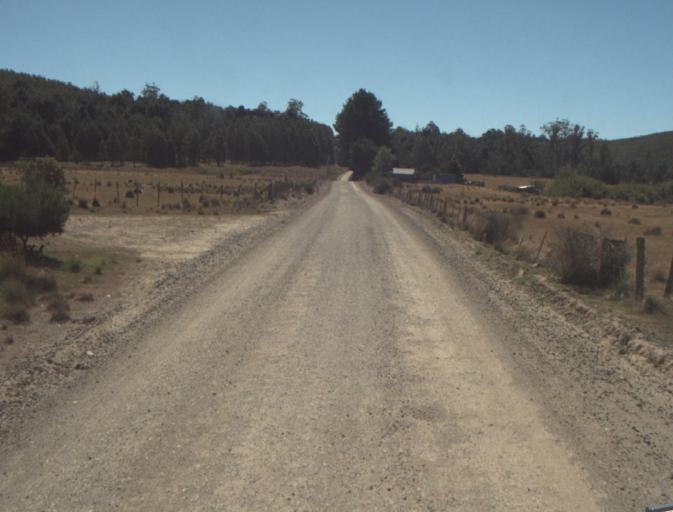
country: AU
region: Tasmania
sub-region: Dorset
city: Scottsdale
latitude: -41.3699
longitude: 147.4704
